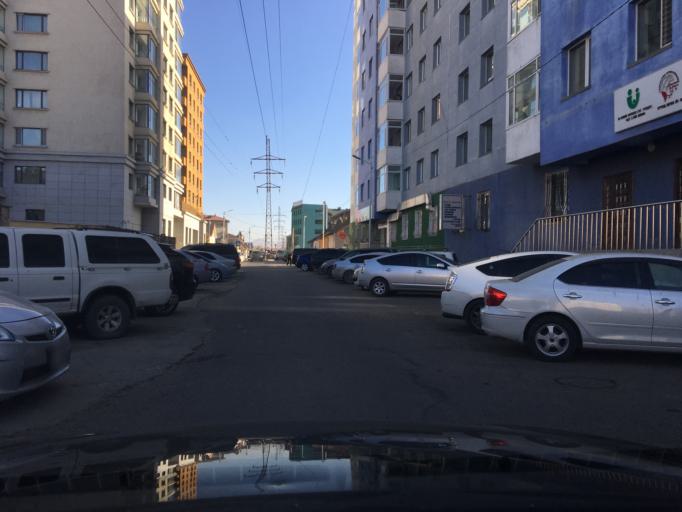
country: MN
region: Ulaanbaatar
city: Ulaanbaatar
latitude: 47.8925
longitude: 106.9058
